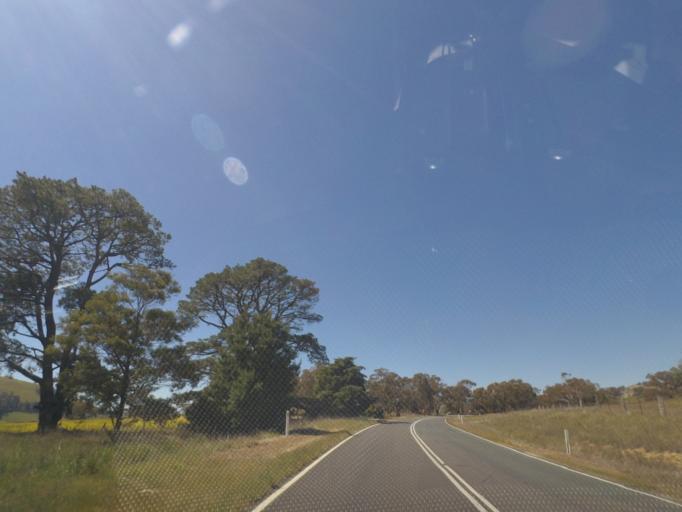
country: AU
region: Victoria
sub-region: Hume
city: Sunbury
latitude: -37.0726
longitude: 144.7724
